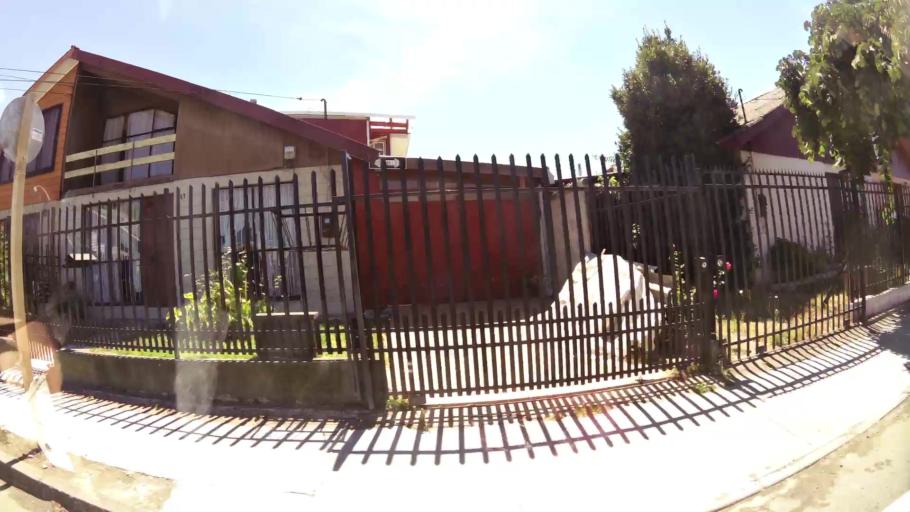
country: CL
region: Biobio
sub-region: Provincia de Concepcion
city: Talcahuano
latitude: -36.7541
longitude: -73.0903
